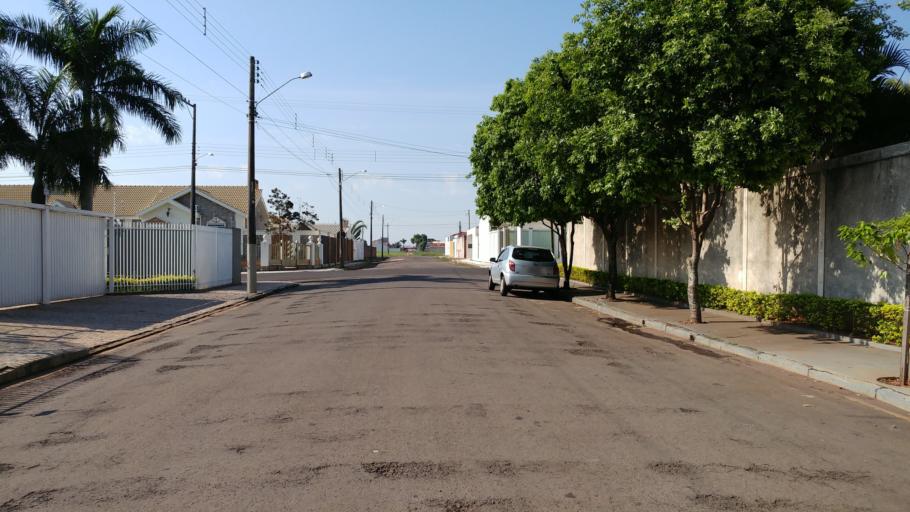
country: BR
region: Sao Paulo
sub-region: Paraguacu Paulista
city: Paraguacu Paulista
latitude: -22.4113
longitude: -50.5848
